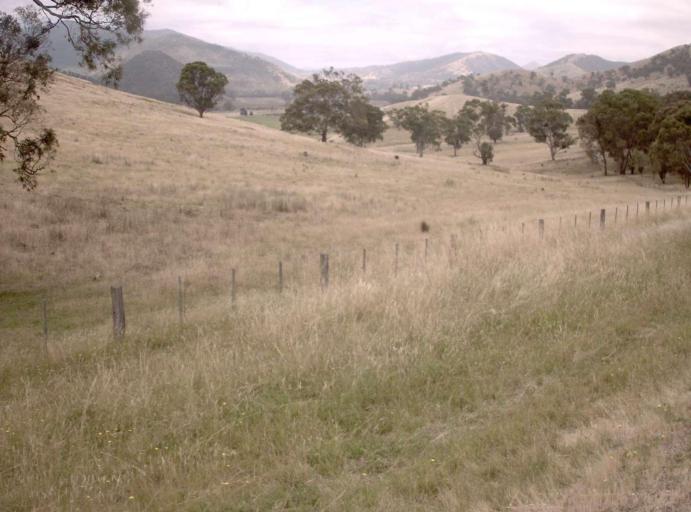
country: AU
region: Victoria
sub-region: Wellington
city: Heyfield
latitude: -37.6854
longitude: 146.6567
